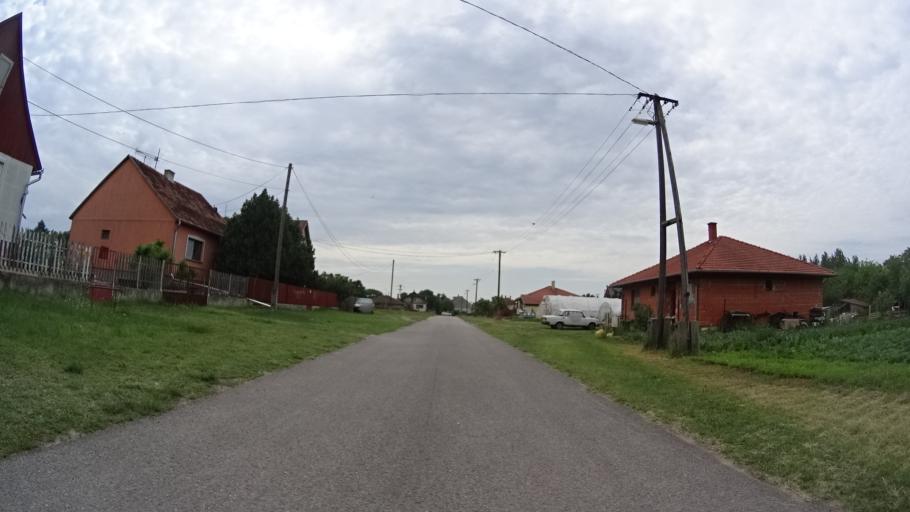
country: HU
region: Bacs-Kiskun
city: Tiszakecske
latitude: 46.9219
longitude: 20.0684
